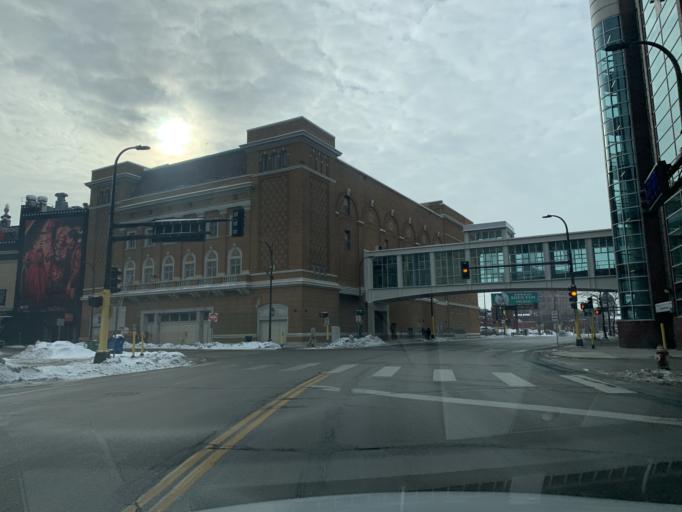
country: US
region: Minnesota
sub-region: Hennepin County
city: Minneapolis
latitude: 44.9774
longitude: -93.2775
